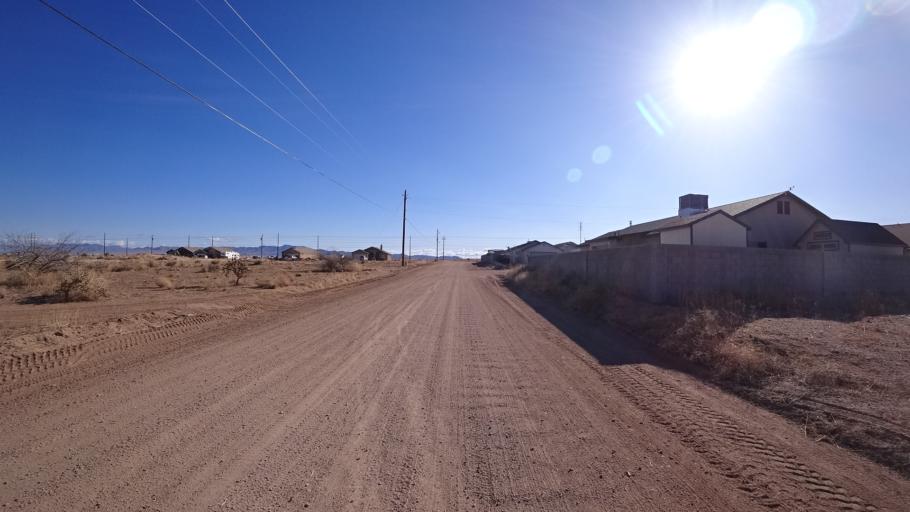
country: US
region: Arizona
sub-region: Mohave County
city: Kingman
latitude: 35.2121
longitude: -113.9956
